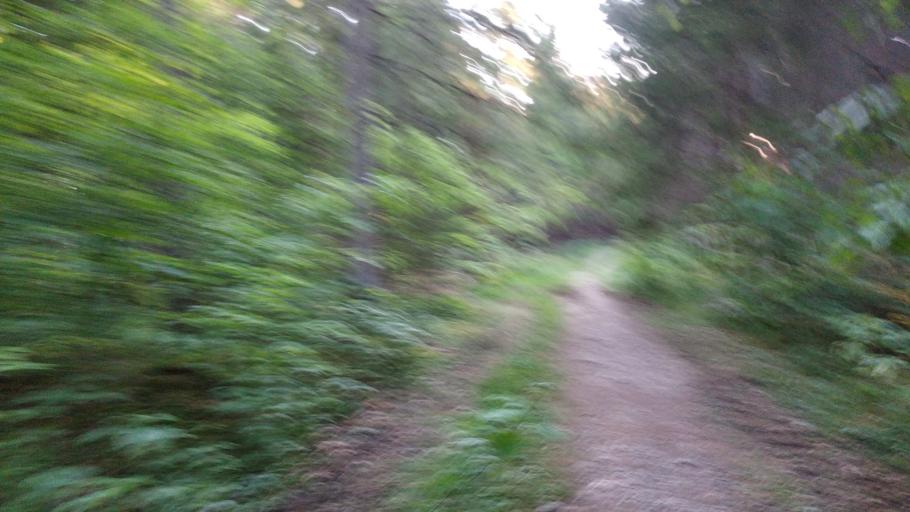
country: DE
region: Bavaria
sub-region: Upper Bavaria
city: Vaterstetten
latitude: 48.0881
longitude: 11.7813
